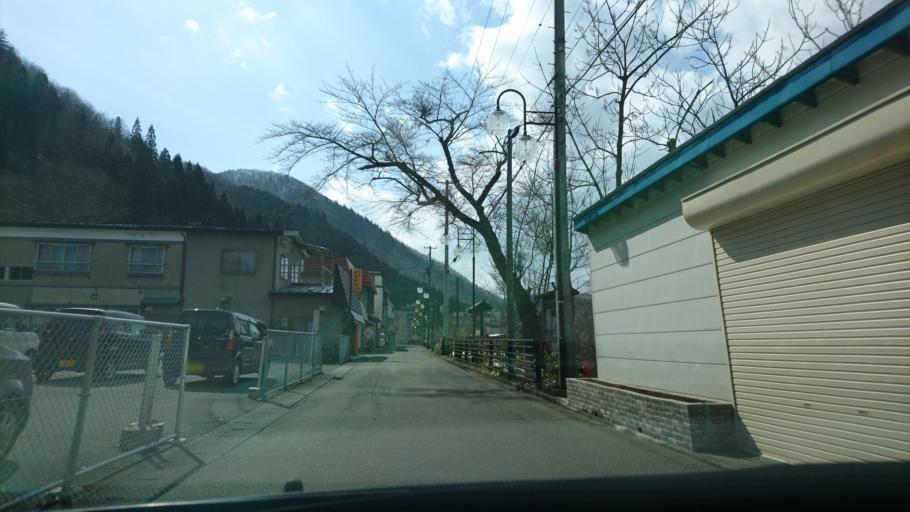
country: JP
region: Iwate
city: Shizukuishi
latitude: 39.6373
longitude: 140.9237
